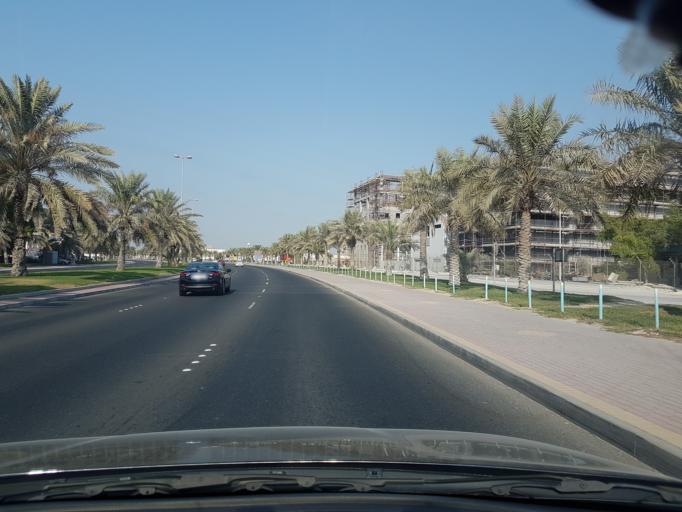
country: BH
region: Muharraq
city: Al Muharraq
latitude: 26.2431
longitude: 50.6163
